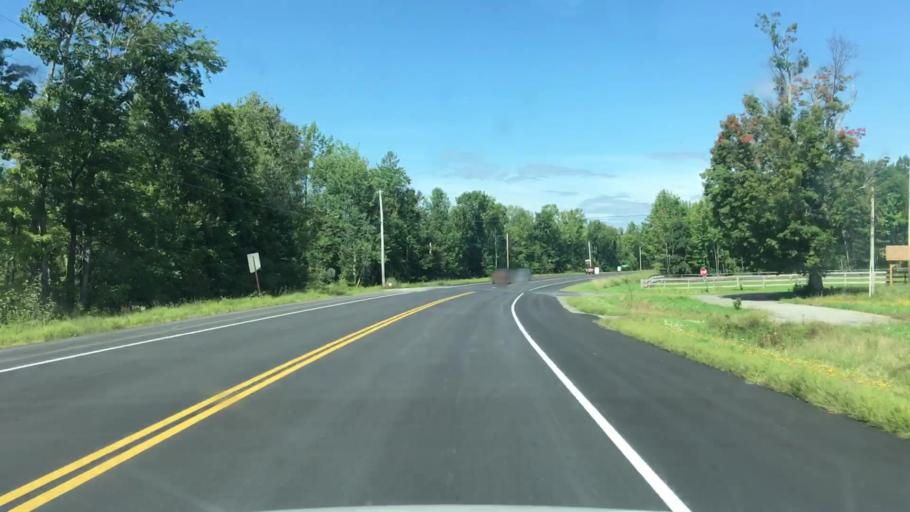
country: US
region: Maine
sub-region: Penobscot County
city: Corinna
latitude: 44.9557
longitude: -69.2618
